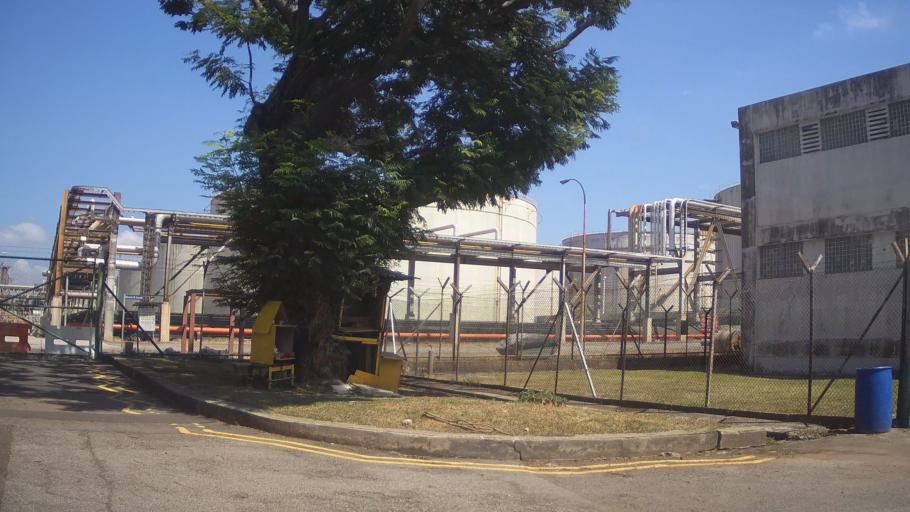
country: SG
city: Singapore
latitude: 1.3084
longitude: 103.6916
